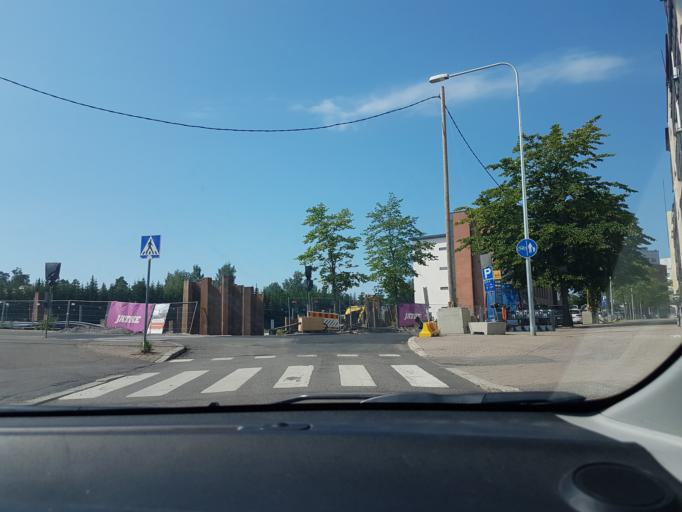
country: FI
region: Uusimaa
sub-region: Helsinki
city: Vantaa
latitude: 60.2055
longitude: 25.1272
